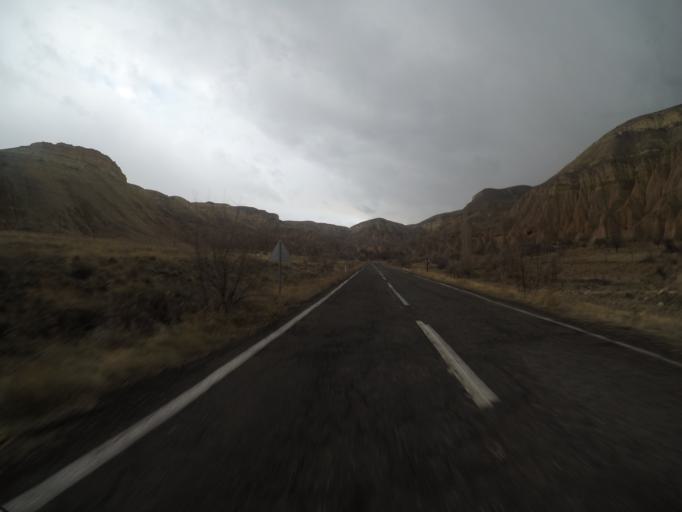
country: TR
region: Nevsehir
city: Goereme
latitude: 38.6743
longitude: 34.8621
